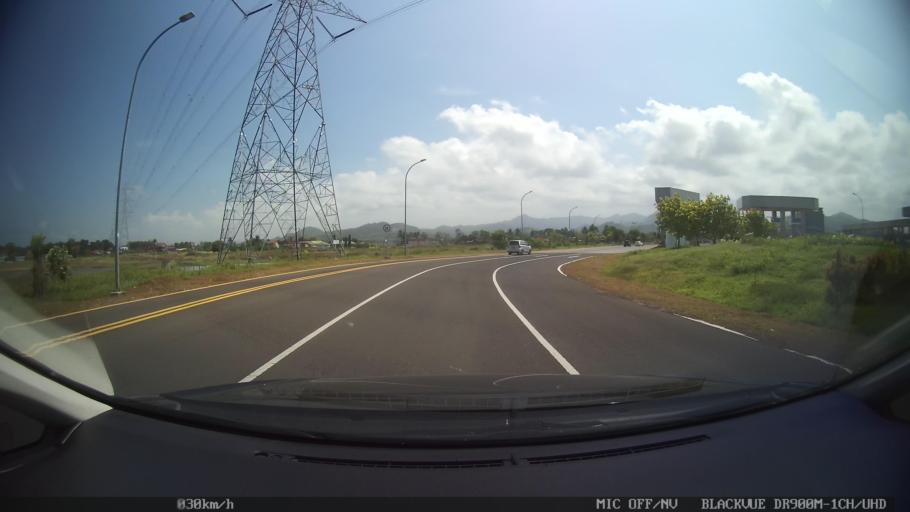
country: ID
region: Daerah Istimewa Yogyakarta
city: Srandakan
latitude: -7.8899
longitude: 110.0621
